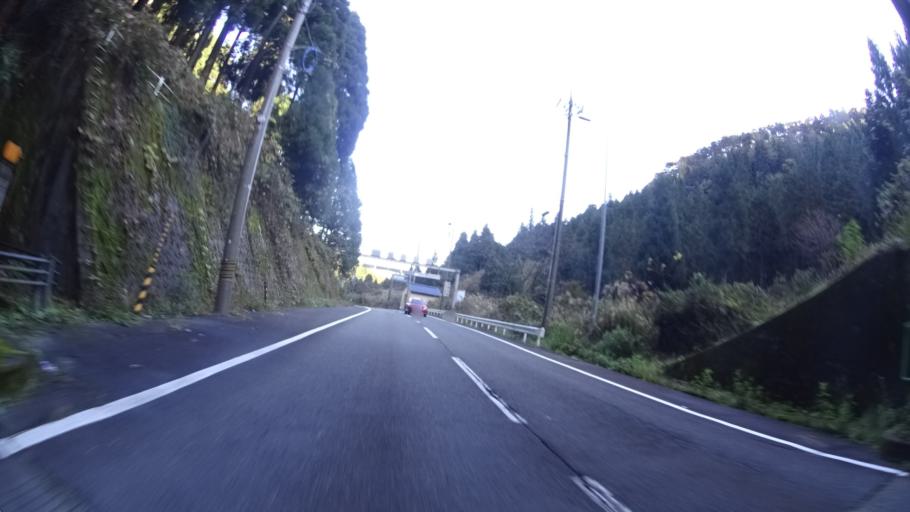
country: JP
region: Fukui
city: Maruoka
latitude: 36.1364
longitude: 136.3248
